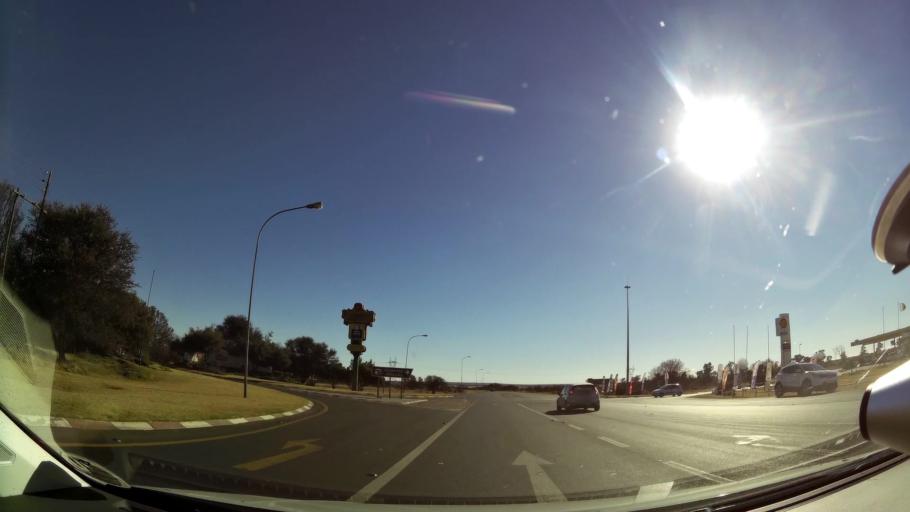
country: ZA
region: Northern Cape
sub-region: Frances Baard District Municipality
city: Kimberley
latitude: -28.6919
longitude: 24.7782
